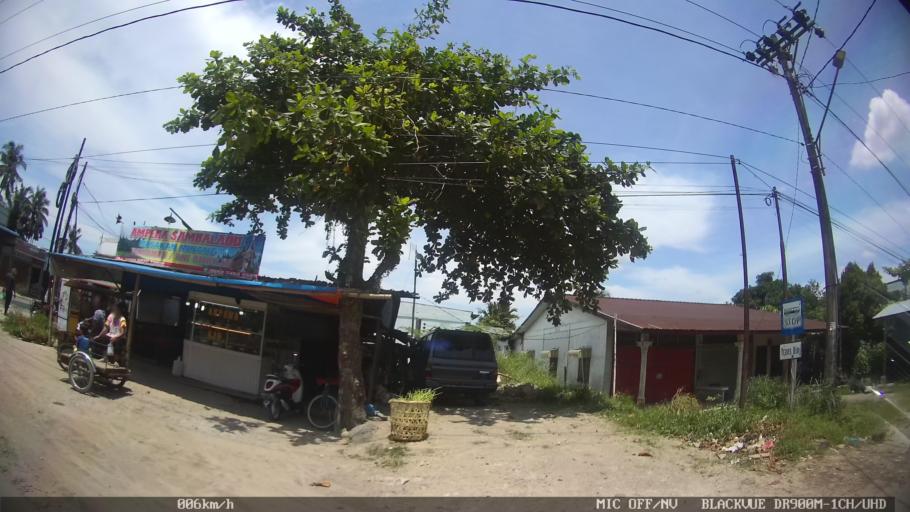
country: ID
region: North Sumatra
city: Binjai
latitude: 3.5913
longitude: 98.5035
